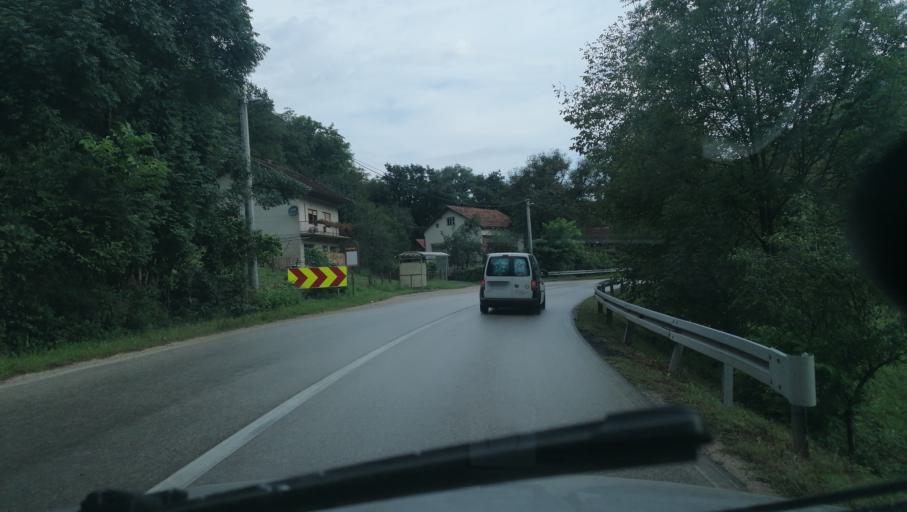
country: BA
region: Republika Srpska
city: Hiseti
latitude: 44.6386
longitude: 17.1455
